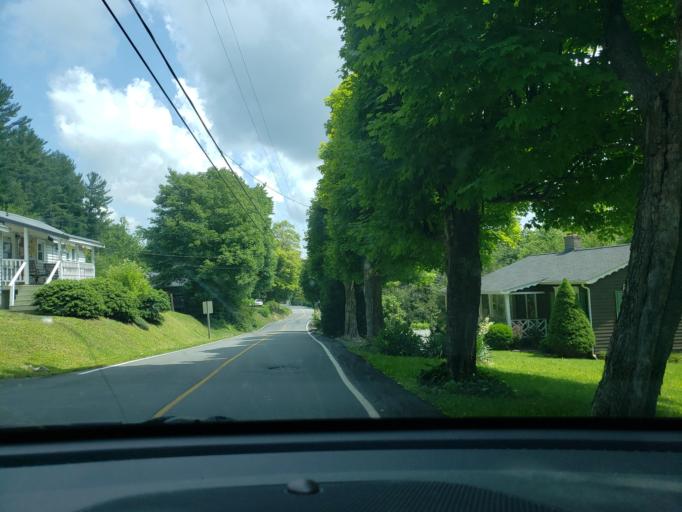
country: US
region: North Carolina
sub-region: Watauga County
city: Blowing Rock
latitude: 36.1253
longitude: -81.6738
